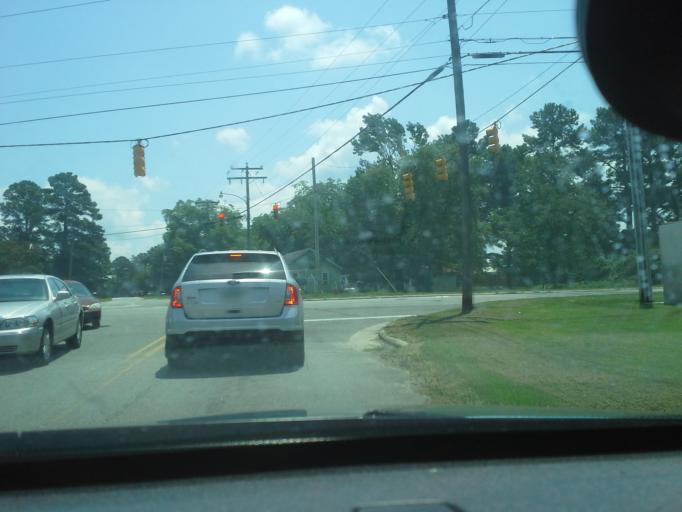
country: US
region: North Carolina
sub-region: Washington County
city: Plymouth
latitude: 35.8540
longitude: -76.7522
